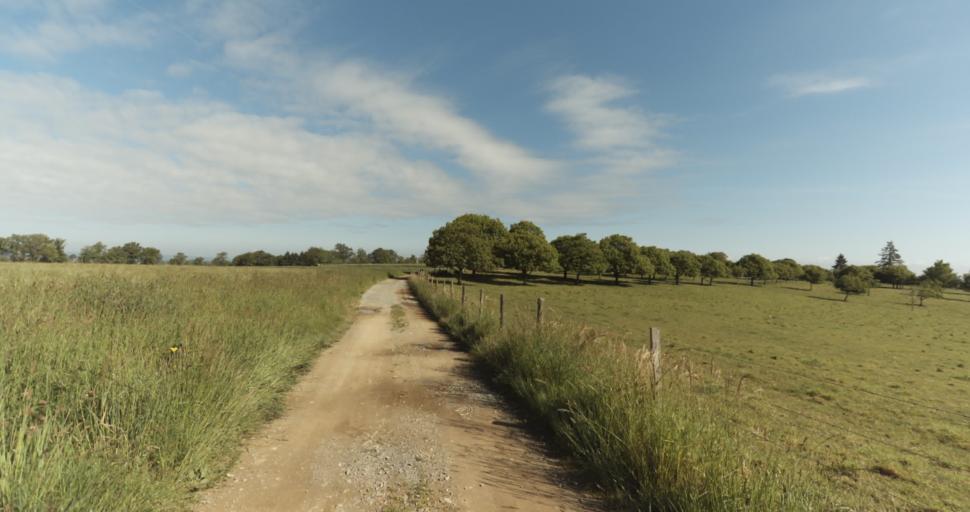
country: FR
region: Limousin
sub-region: Departement de la Haute-Vienne
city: Solignac
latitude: 45.7221
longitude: 1.2435
